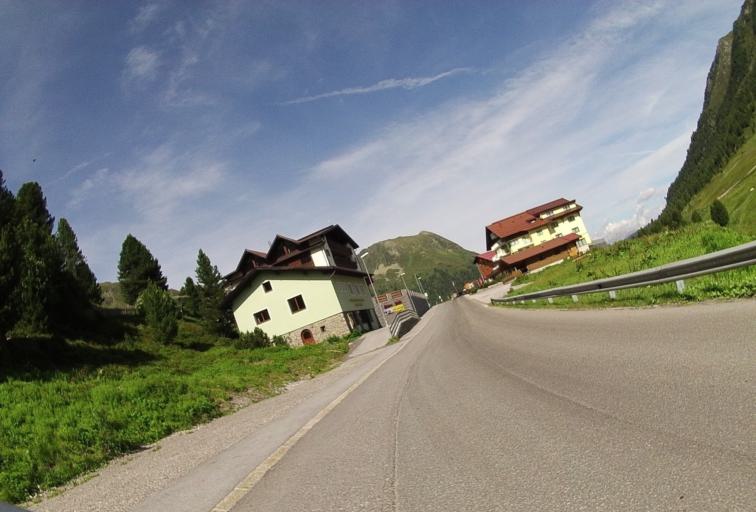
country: AT
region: Tyrol
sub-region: Politischer Bezirk Imst
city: Stams
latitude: 47.2116
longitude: 11.0100
